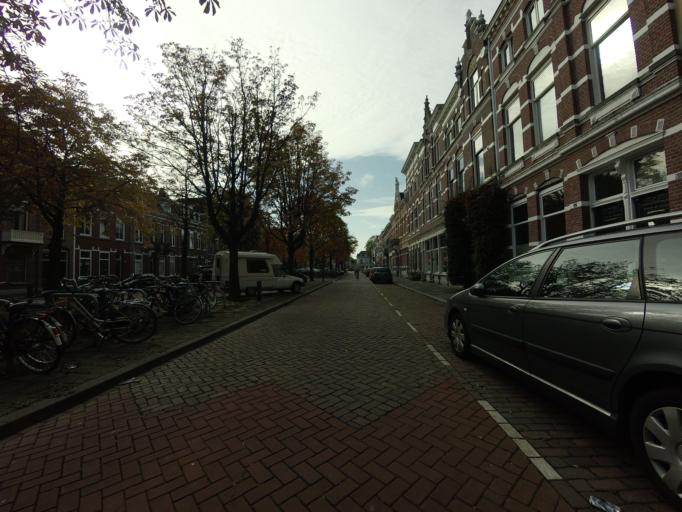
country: NL
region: North Brabant
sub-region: Gemeente Breda
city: Breda
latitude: 51.5925
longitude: 4.7869
